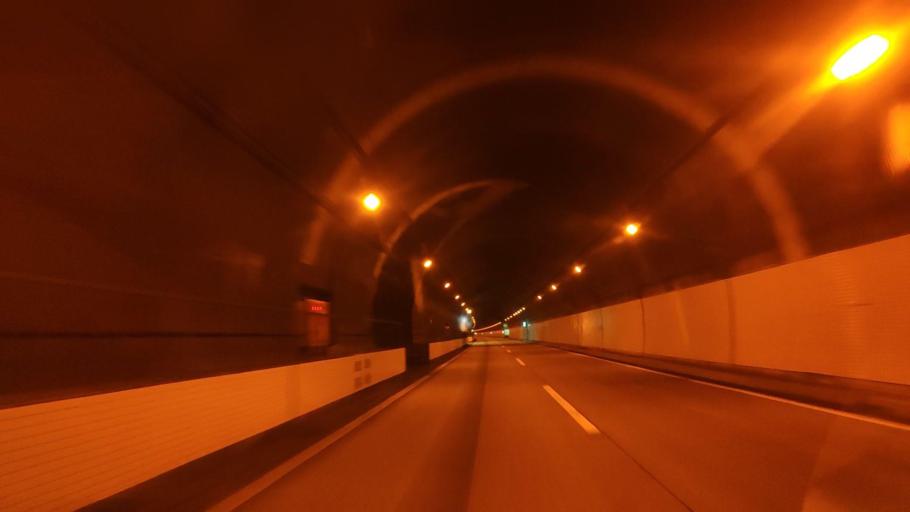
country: JP
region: Toyama
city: Nyuzen
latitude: 36.9785
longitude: 137.6594
